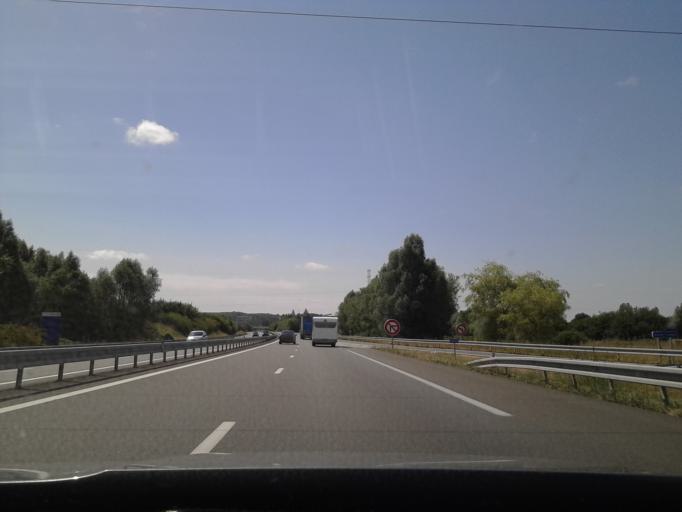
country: FR
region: Pays de la Loire
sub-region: Departement de la Sarthe
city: Teloche
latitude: 47.8815
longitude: 0.3040
